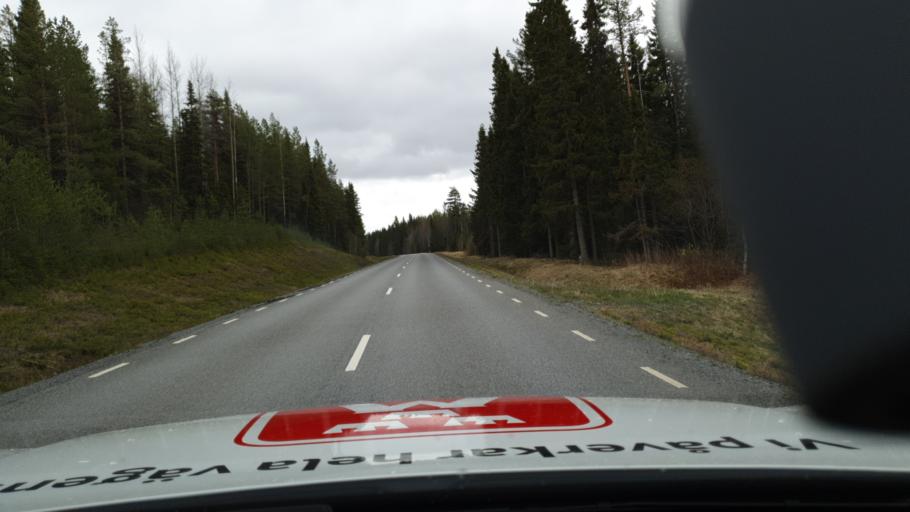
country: SE
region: Jaemtland
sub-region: Stroemsunds Kommun
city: Stroemsund
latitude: 63.6382
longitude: 15.1910
